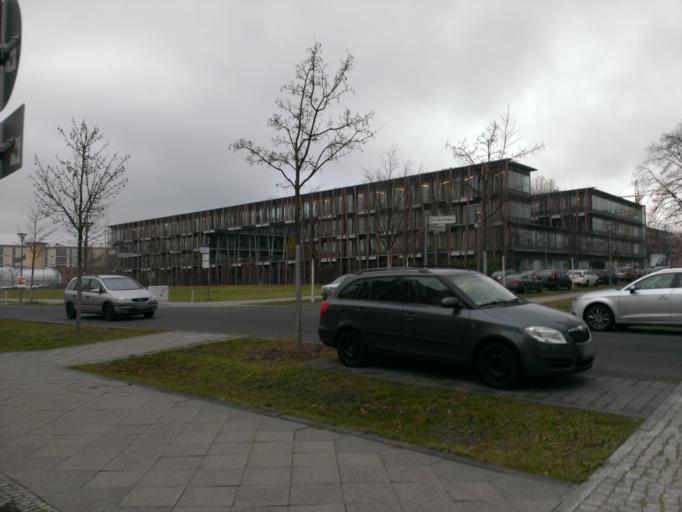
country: DE
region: Berlin
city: Adlershof
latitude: 52.4331
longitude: 13.5322
